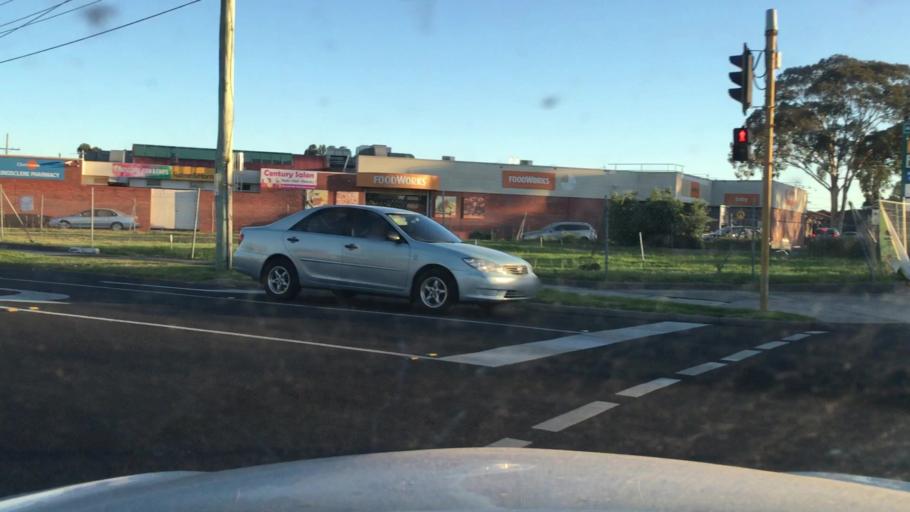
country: AU
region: Victoria
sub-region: Greater Dandenong
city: Noble Park
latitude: -37.9800
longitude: 145.1656
